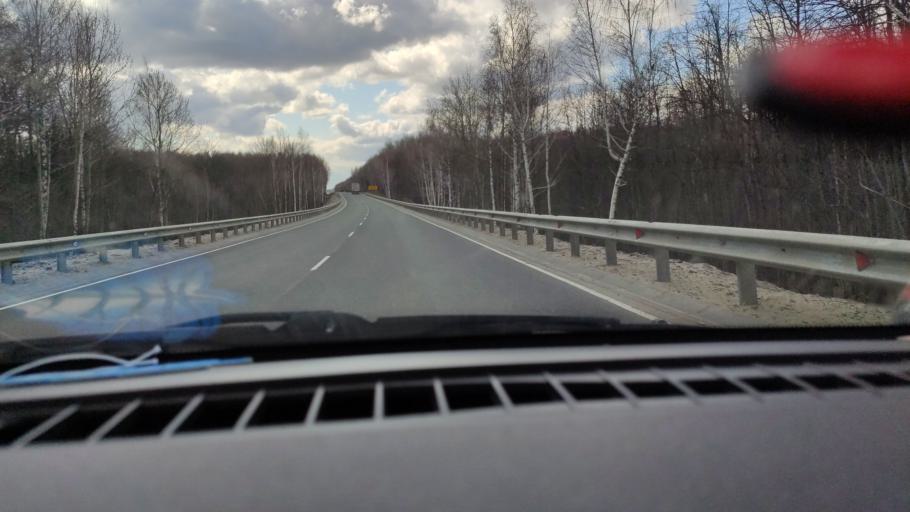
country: RU
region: Saratov
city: Khvalynsk
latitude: 52.4389
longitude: 48.0093
